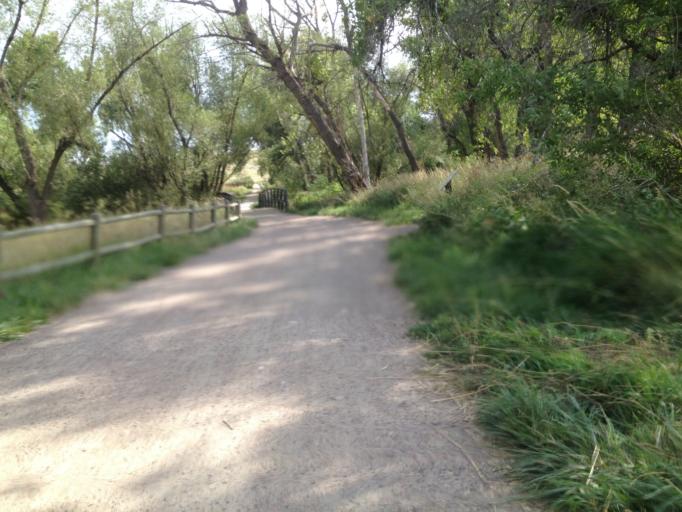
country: US
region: Colorado
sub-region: Boulder County
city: Louisville
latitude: 39.9780
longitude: -105.1139
